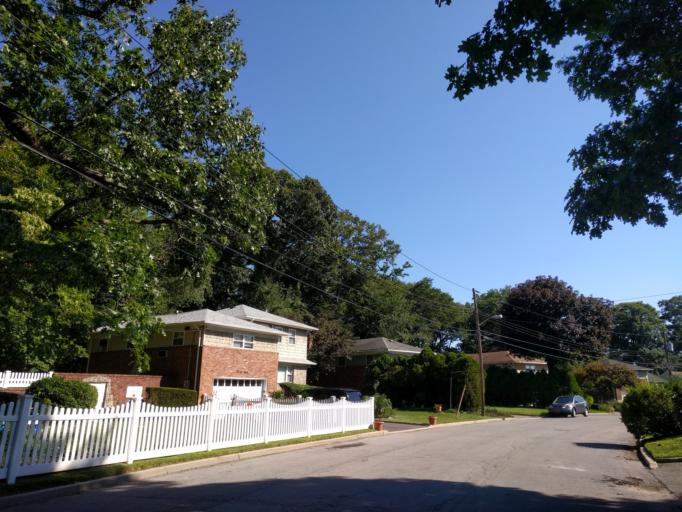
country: US
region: New York
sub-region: Nassau County
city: Locust Valley
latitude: 40.8759
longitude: -73.6151
